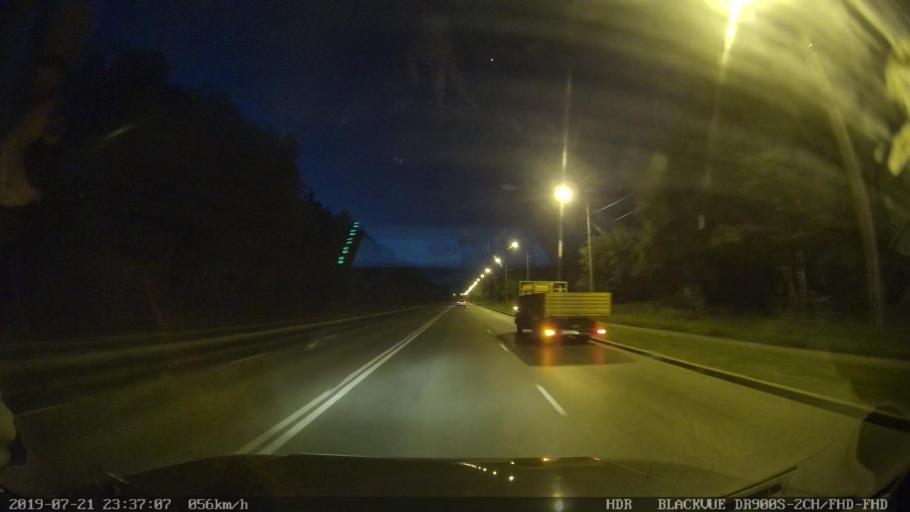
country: RU
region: Perm
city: Kondratovo
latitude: 57.9451
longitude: 56.1723
